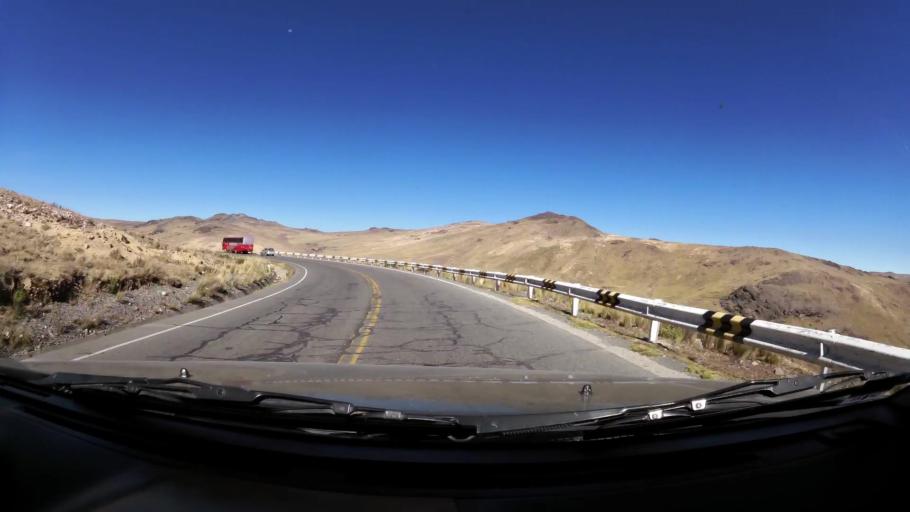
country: PE
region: Huancavelica
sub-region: Huaytara
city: Huayacundo Arma
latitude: -13.5525
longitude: -75.2210
